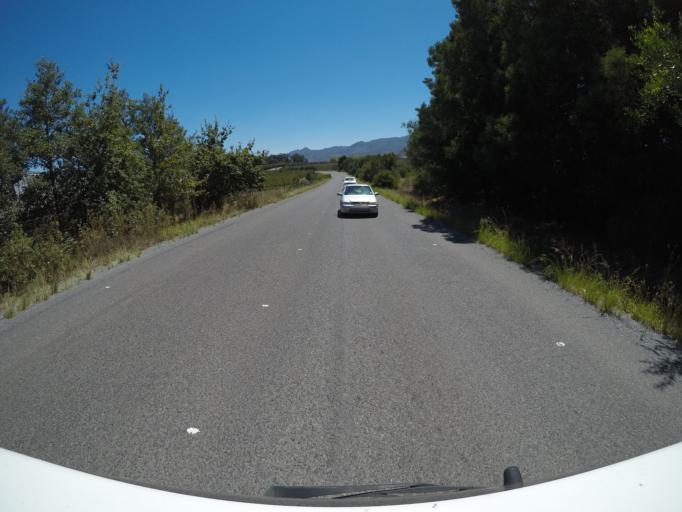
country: ZA
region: Western Cape
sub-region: Overberg District Municipality
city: Grabouw
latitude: -34.1706
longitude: 19.0351
